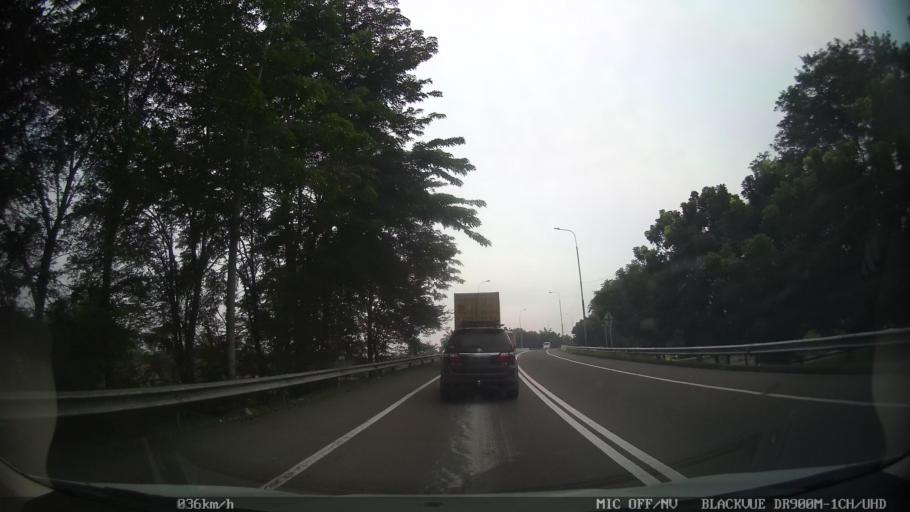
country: ID
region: North Sumatra
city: Deli Tua
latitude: 3.5445
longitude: 98.7267
